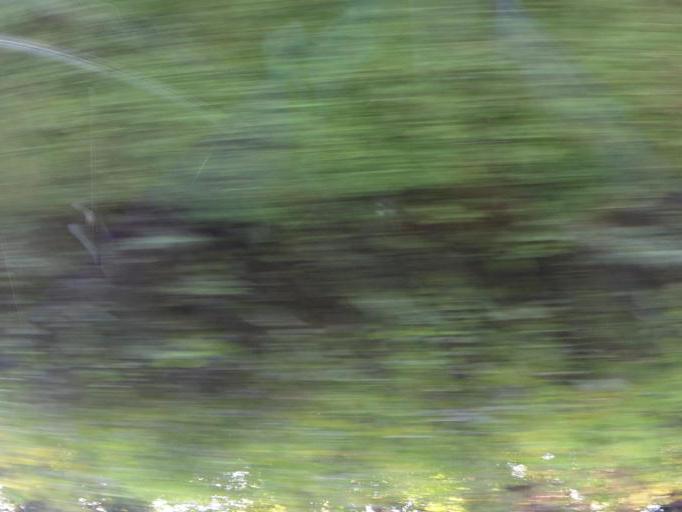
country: US
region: Tennessee
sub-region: Union County
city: Condon
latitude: 36.1781
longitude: -83.8109
